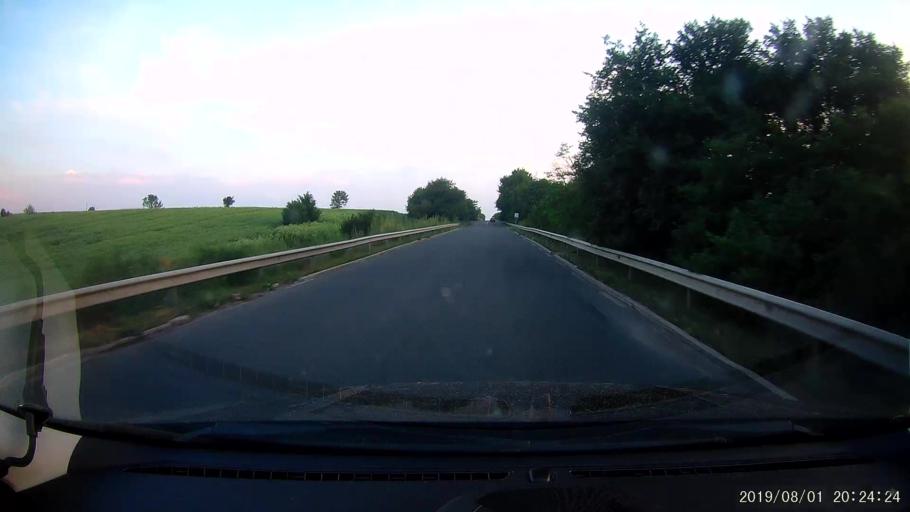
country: BG
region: Yambol
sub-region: Obshtina Elkhovo
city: Elkhovo
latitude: 42.2323
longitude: 26.5938
